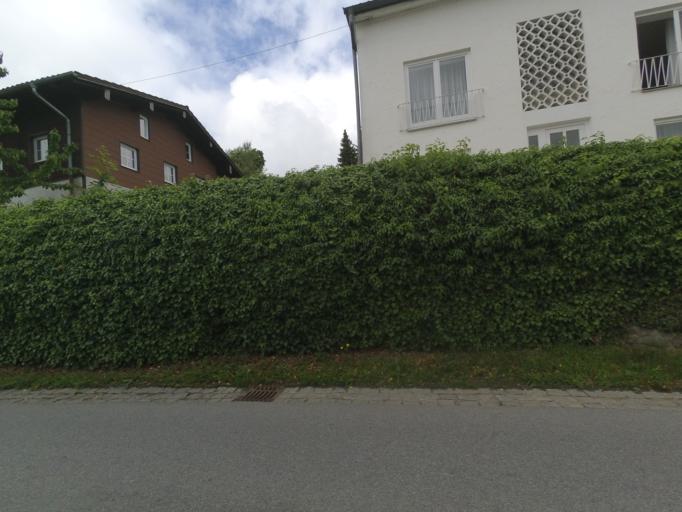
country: DE
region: Bavaria
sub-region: Lower Bavaria
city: Konzell
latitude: 49.0734
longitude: 12.7134
